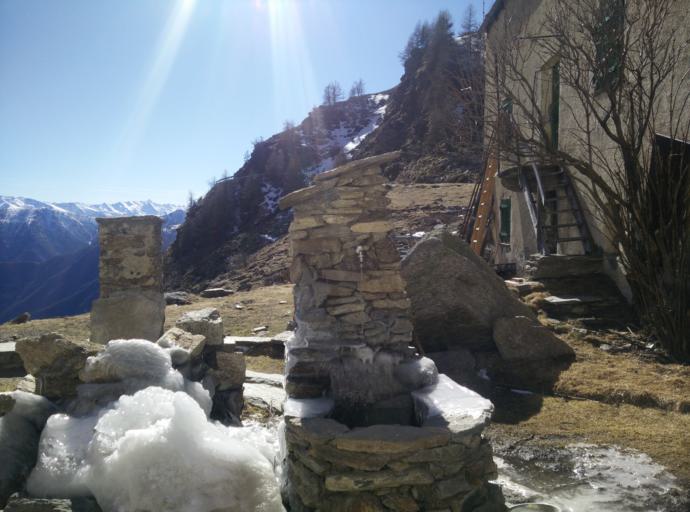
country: IT
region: Piedmont
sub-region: Provincia di Torino
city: Roure
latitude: 45.0475
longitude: 7.1203
